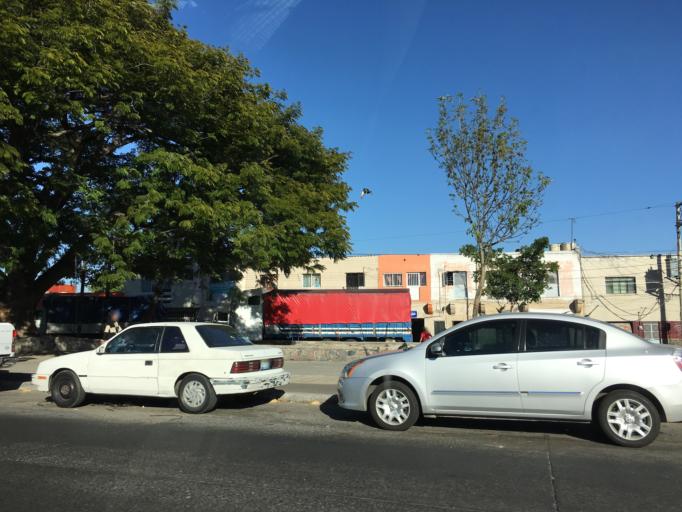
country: MX
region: Jalisco
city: Guadalajara
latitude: 20.6906
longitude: -103.3538
